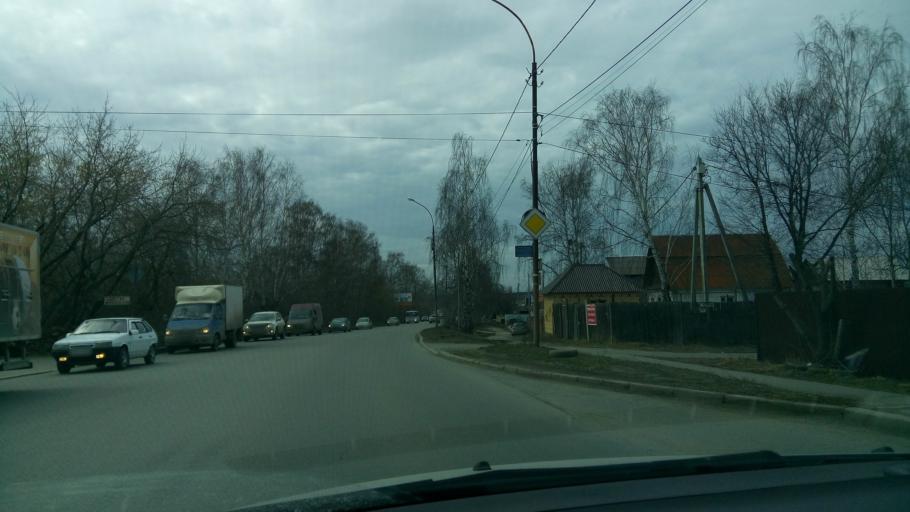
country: RU
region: Sverdlovsk
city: Beryozovsky
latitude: 56.8849
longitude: 60.7222
